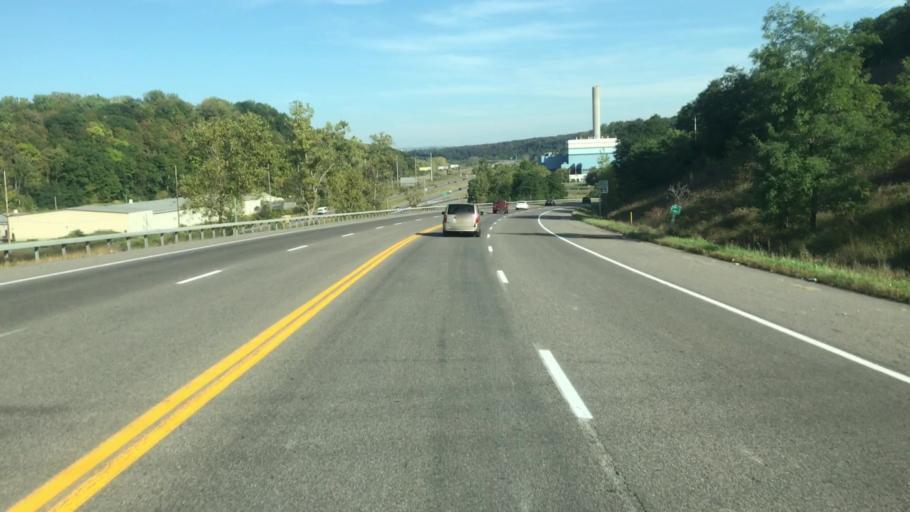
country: US
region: New York
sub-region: Onondaga County
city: Nedrow
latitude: 43.0069
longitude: -76.1245
